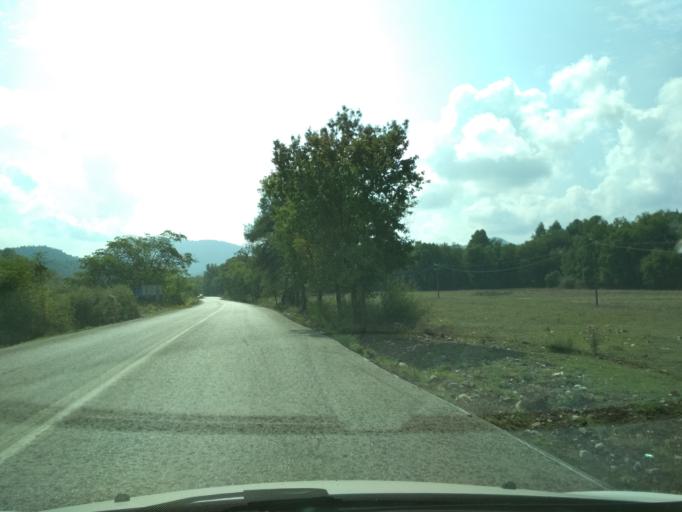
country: GR
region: Central Greece
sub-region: Nomos Evvoias
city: Prokopion
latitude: 38.7316
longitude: 23.4982
